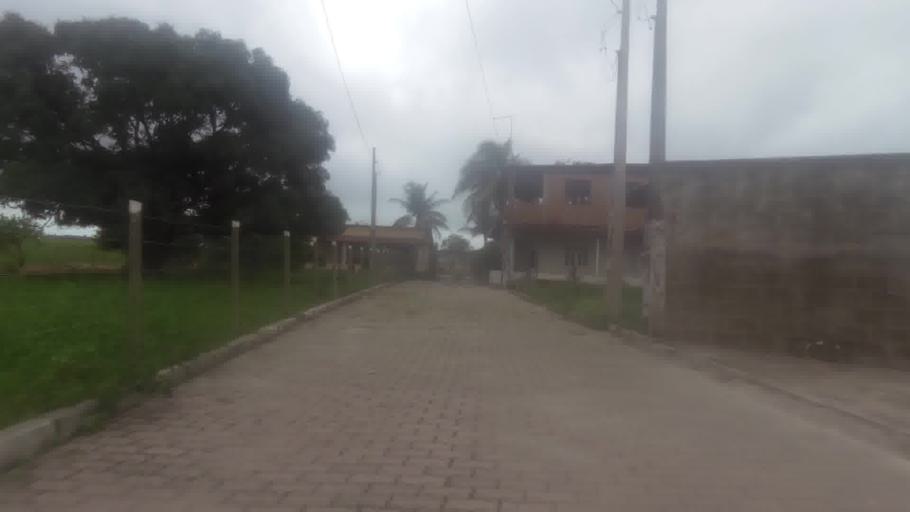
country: BR
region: Espirito Santo
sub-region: Piuma
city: Piuma
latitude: -20.7941
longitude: -40.6015
